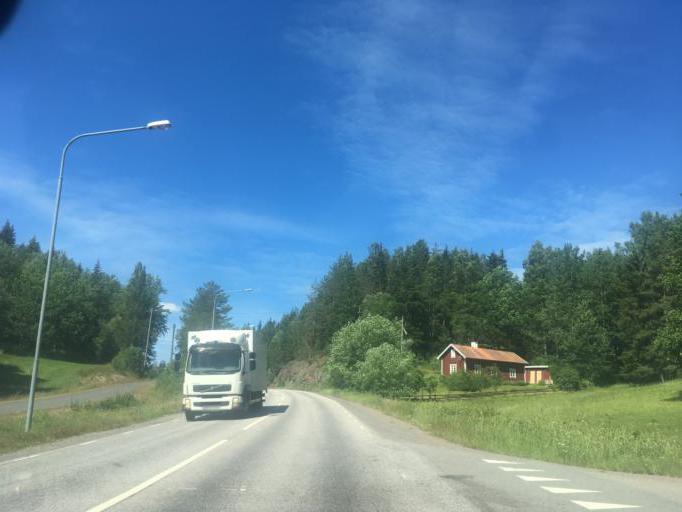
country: SE
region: OEstergoetland
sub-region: Valdemarsviks Kommun
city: Valdemarsvik
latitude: 58.2183
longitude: 16.5745
